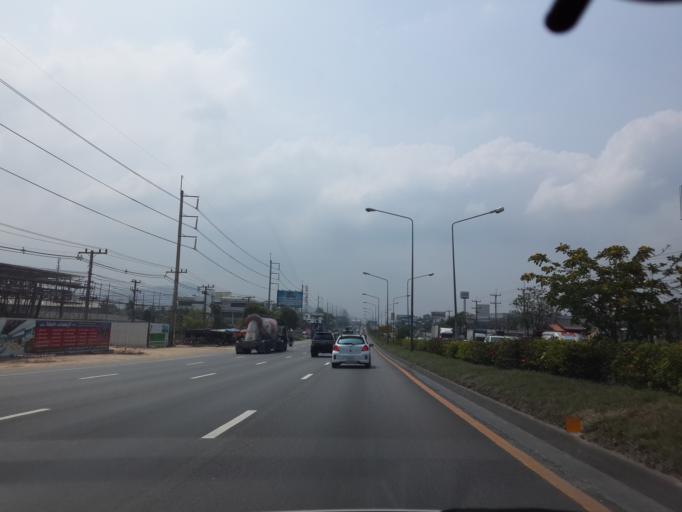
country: TH
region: Chon Buri
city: Chon Buri
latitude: 13.3737
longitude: 101.0195
